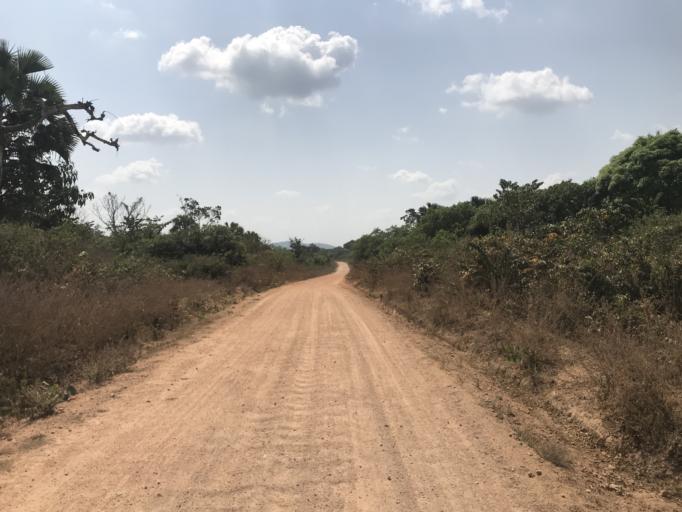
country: NG
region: Osun
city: Ifon
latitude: 7.9438
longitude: 4.4895
